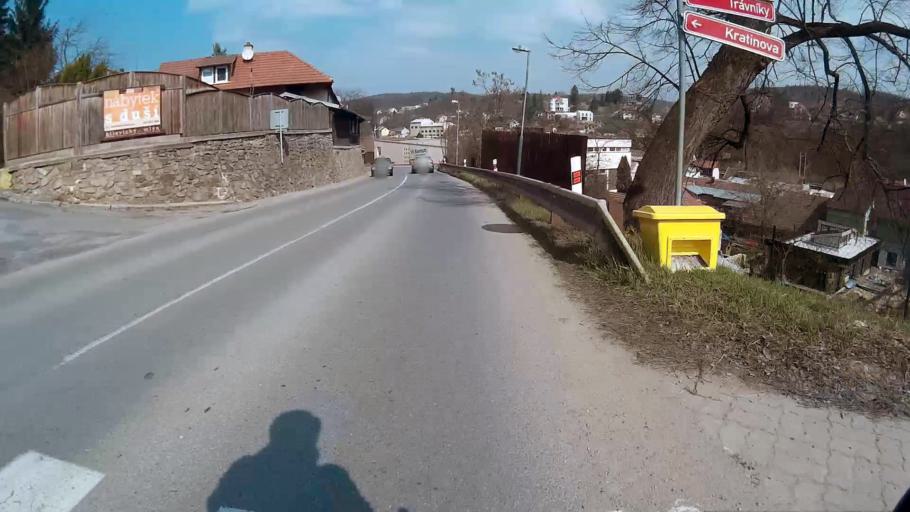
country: CZ
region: South Moravian
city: Bilovice nad Svitavou
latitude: 49.2459
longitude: 16.6721
